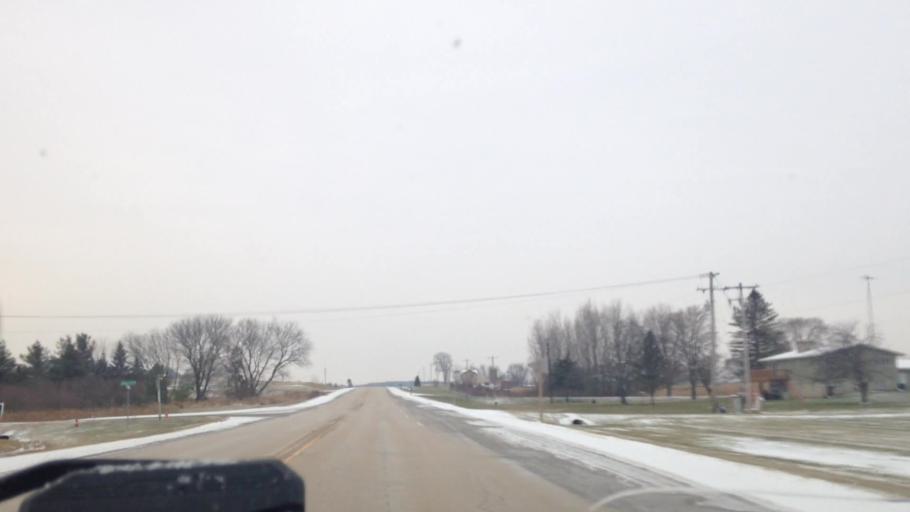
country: US
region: Wisconsin
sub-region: Dodge County
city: Mayville
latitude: 43.4801
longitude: -88.5460
